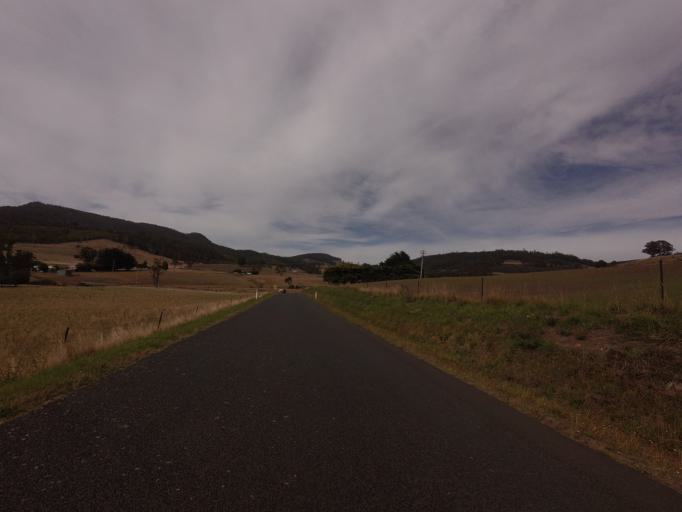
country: AU
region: Tasmania
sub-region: Sorell
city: Sorell
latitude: -42.4799
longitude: 147.5748
